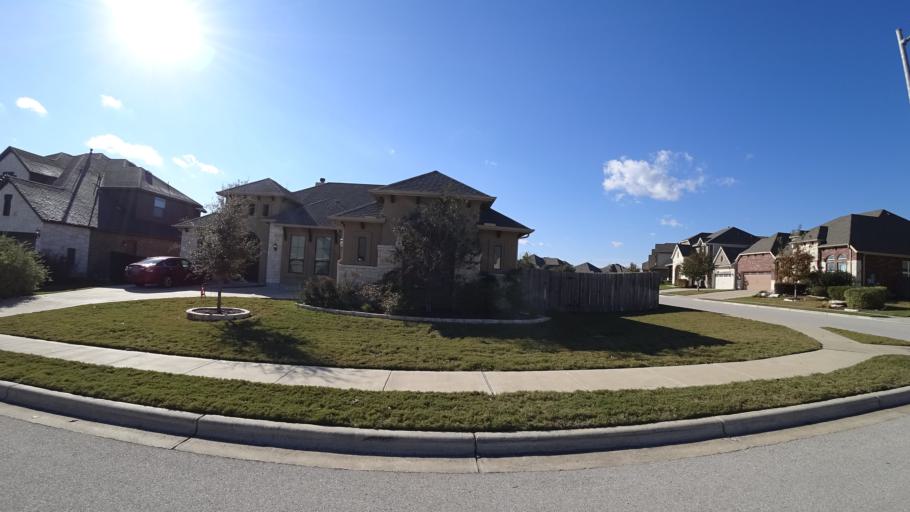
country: US
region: Texas
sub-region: Williamson County
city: Brushy Creek
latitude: 30.4867
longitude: -97.7249
